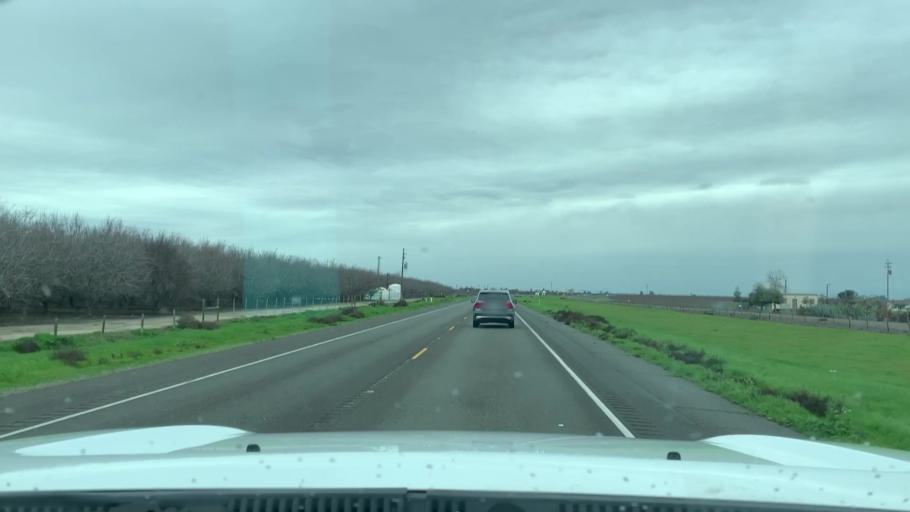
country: US
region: California
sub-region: Fresno County
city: Caruthers
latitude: 36.4803
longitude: -119.7924
